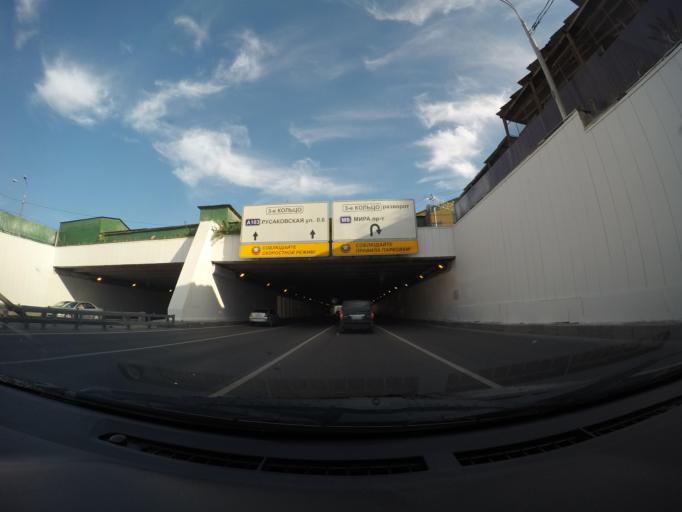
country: RU
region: Moscow
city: Sokol'niki
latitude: 55.7881
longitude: 37.6598
